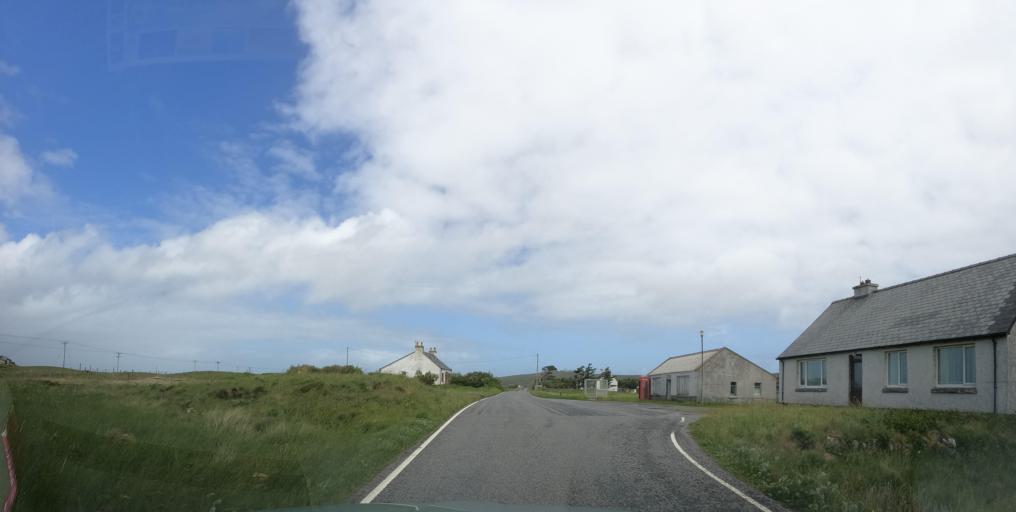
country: GB
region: Scotland
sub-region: Eilean Siar
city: Isle of South Uist
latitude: 57.3233
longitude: -7.3680
